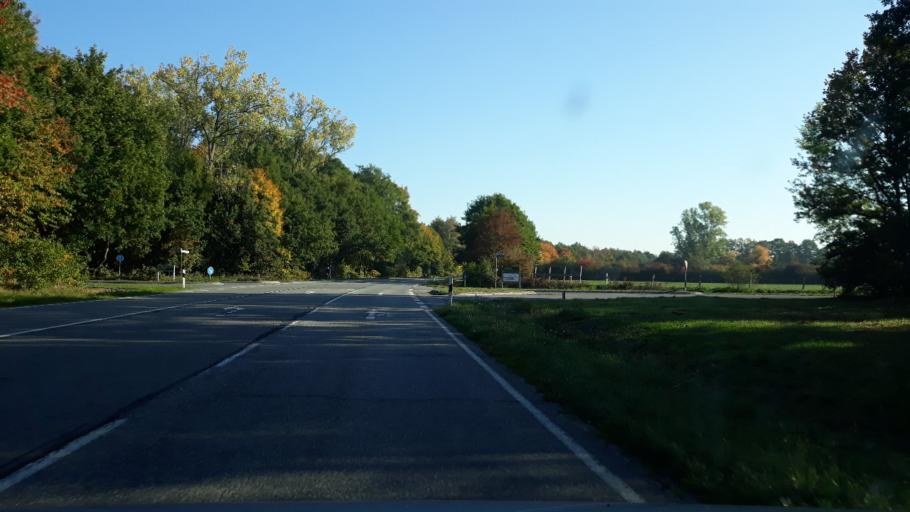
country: DE
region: Schleswig-Holstein
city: Kropp
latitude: 54.4051
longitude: 9.5247
